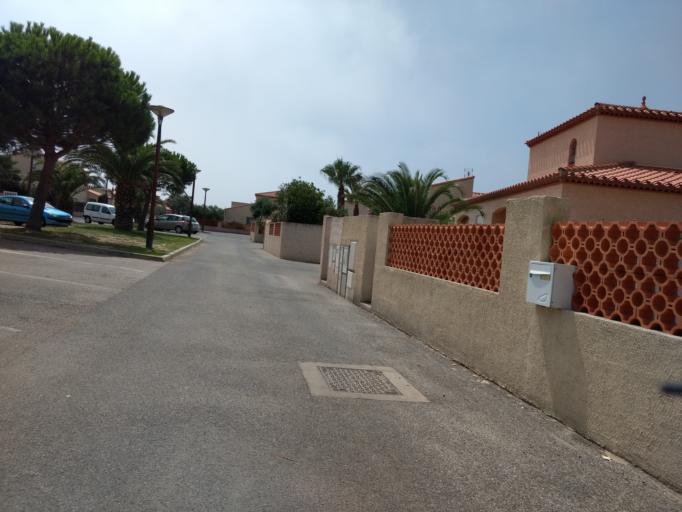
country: FR
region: Languedoc-Roussillon
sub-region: Departement des Pyrenees-Orientales
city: Le Barcares
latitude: 42.8085
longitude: 3.0325
